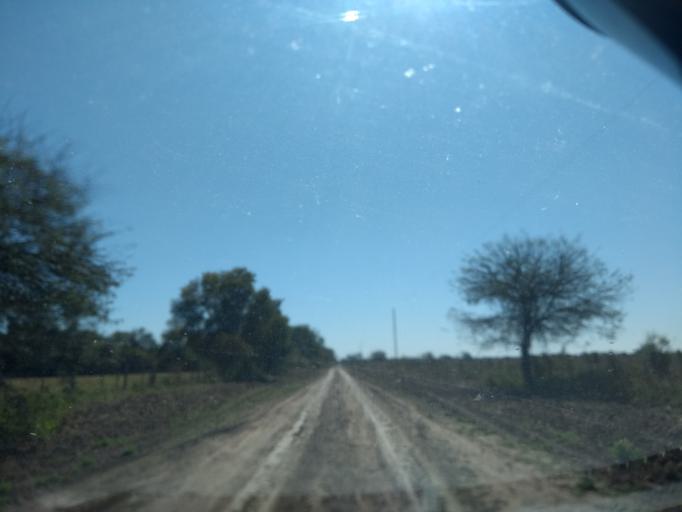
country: AR
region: Chaco
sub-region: Departamento de Quitilipi
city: Quitilipi
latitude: -26.7400
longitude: -60.2358
